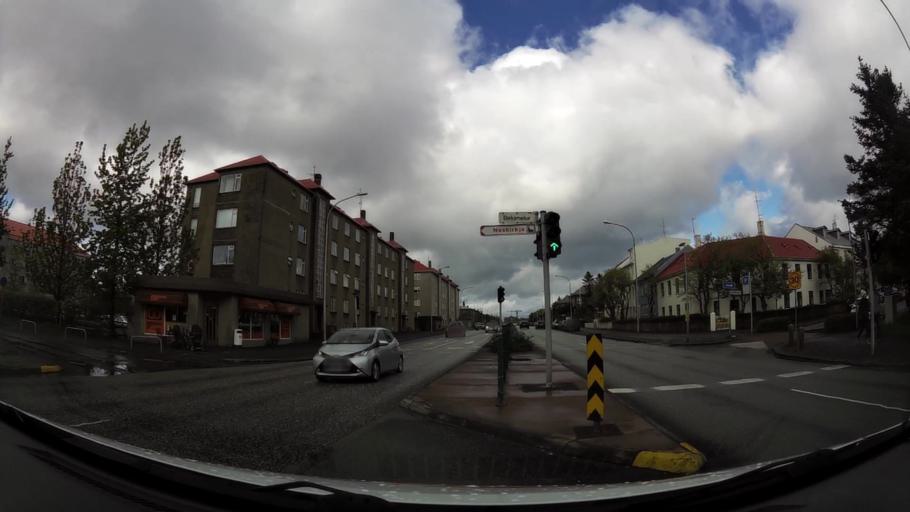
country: IS
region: Capital Region
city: Seltjarnarnes
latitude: 64.1439
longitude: -21.9505
